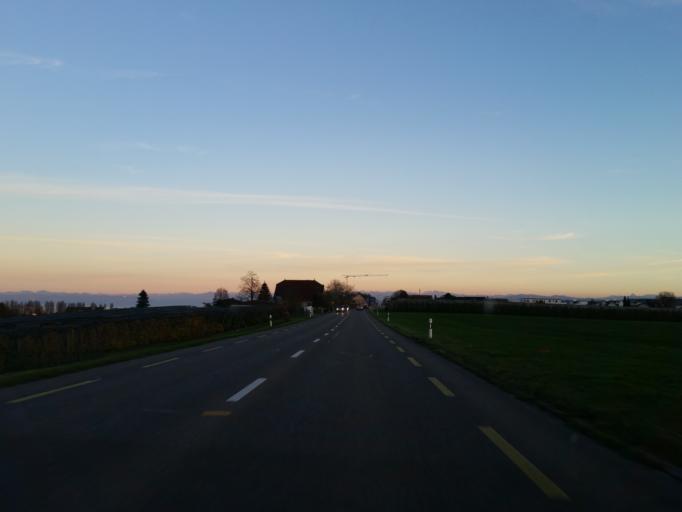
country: CH
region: Thurgau
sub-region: Kreuzlingen District
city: Altnau
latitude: 47.6220
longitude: 9.2599
